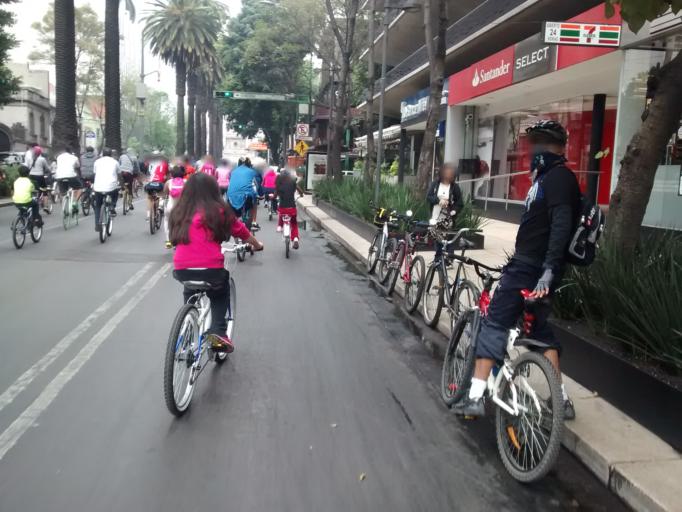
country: MX
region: Mexico City
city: Benito Juarez
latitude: 19.4249
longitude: -99.1664
